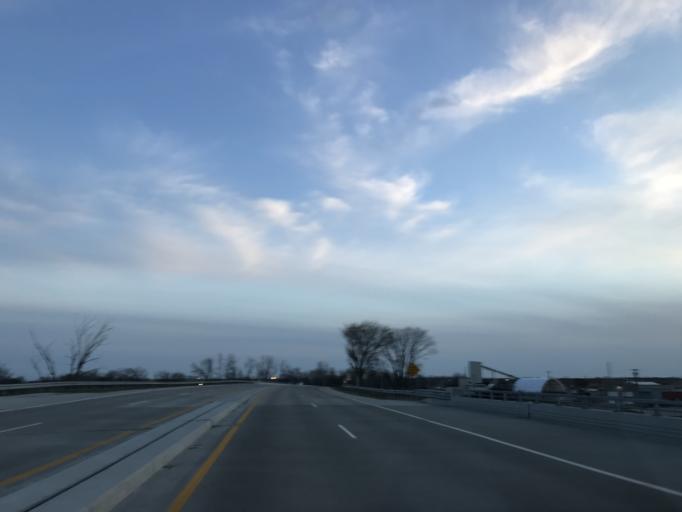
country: US
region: Michigan
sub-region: Wayne County
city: Southgate
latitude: 42.1845
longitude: -83.2267
